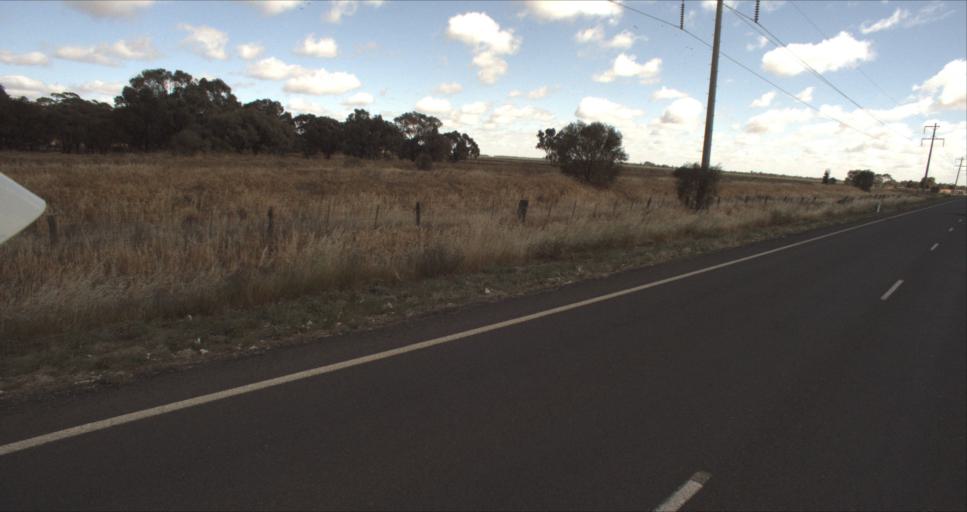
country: AU
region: New South Wales
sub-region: Murrumbidgee Shire
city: Darlington Point
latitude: -34.5432
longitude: 146.1717
